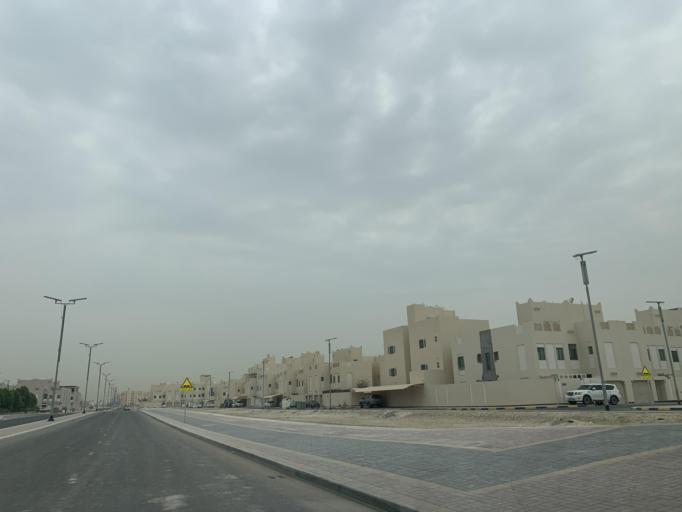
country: BH
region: Northern
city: Madinat `Isa
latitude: 26.1778
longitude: 50.5135
